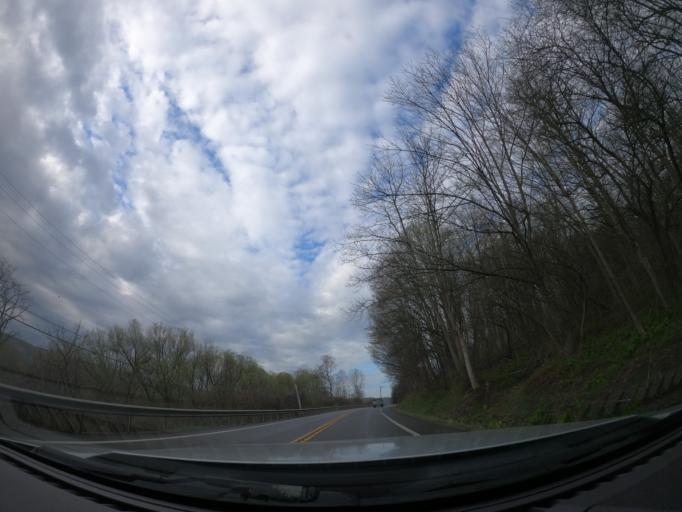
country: US
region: New York
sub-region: Cortland County
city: McGraw
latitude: 42.6876
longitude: -76.0517
